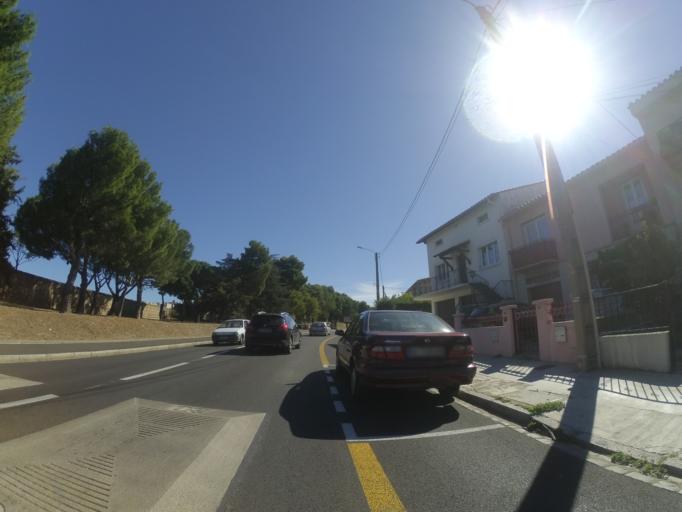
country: FR
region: Languedoc-Roussillon
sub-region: Departement des Pyrenees-Orientales
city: Perpignan
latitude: 42.6855
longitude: 2.8887
